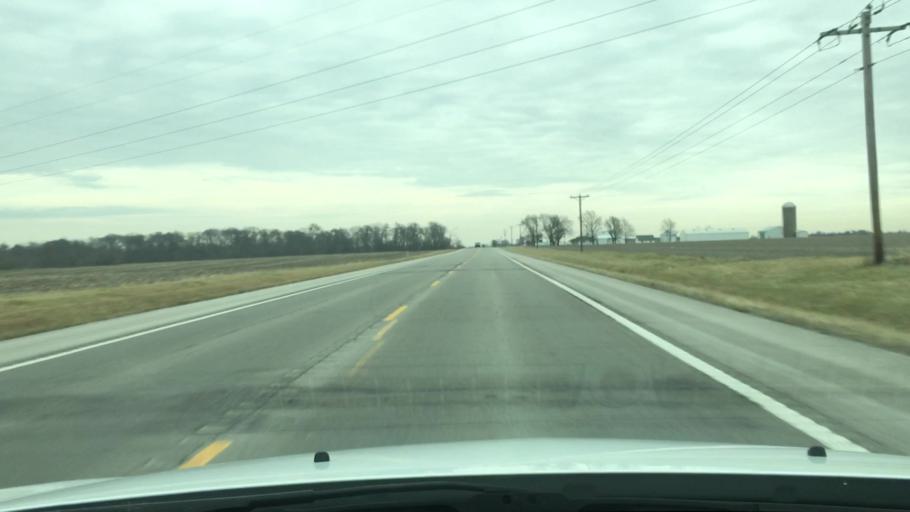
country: US
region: Missouri
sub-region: Audrain County
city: Mexico
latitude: 39.1638
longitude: -91.7574
